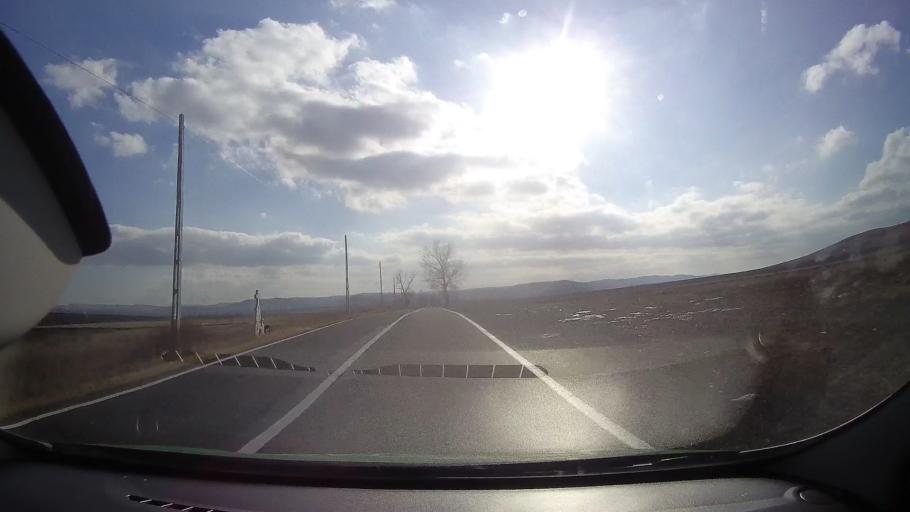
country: RO
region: Tulcea
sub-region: Comuna Nalbant
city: Nicolae Balcescu
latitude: 45.0144
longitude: 28.5998
